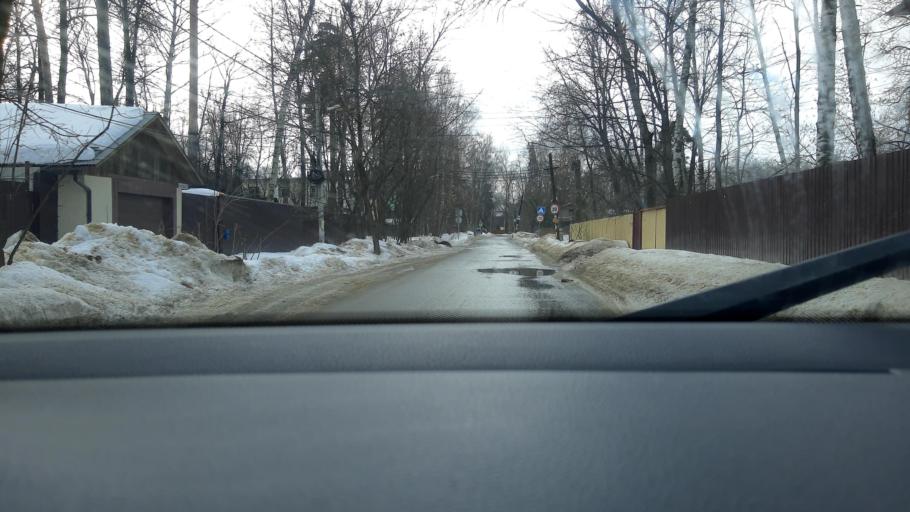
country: RU
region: Moskovskaya
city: Druzhba
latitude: 55.8956
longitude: 37.7376
